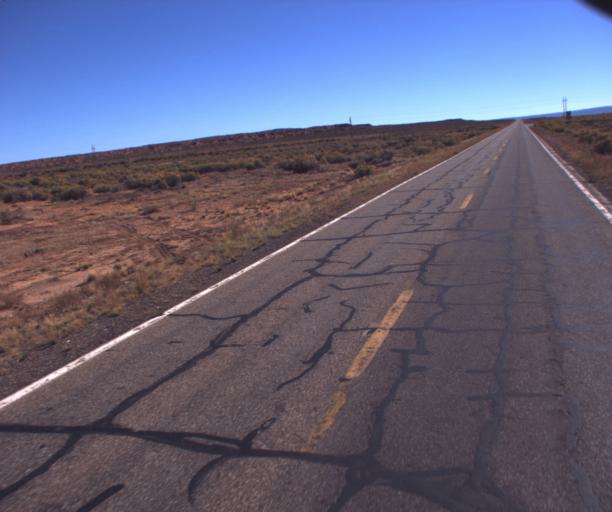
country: US
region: Arizona
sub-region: Coconino County
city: Fredonia
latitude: 36.9355
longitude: -112.5084
